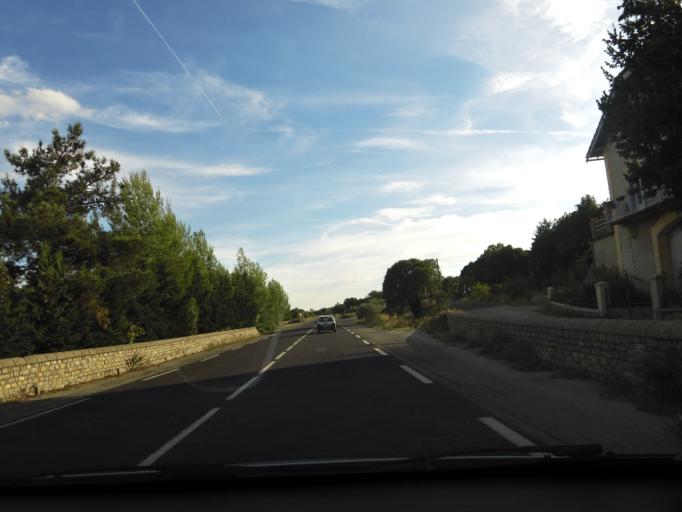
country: FR
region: Languedoc-Roussillon
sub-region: Departement de l'Herault
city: Claret
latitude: 43.8611
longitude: 3.9359
